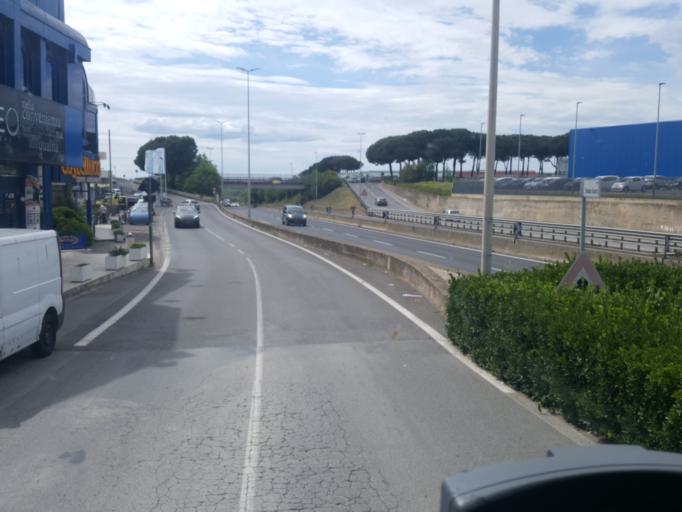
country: IT
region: Latium
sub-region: Citta metropolitana di Roma Capitale
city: La Massimina-Casal Lumbroso
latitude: 41.8815
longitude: 12.3489
